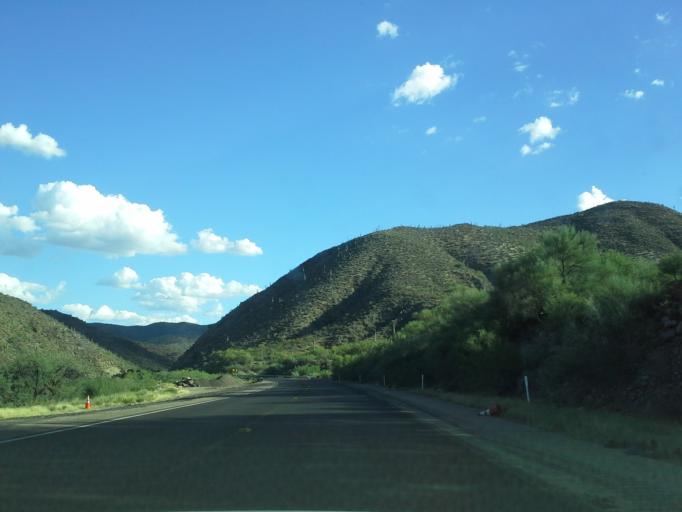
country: US
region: Arizona
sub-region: Pinal County
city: Kearny
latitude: 33.0621
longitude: -110.7238
